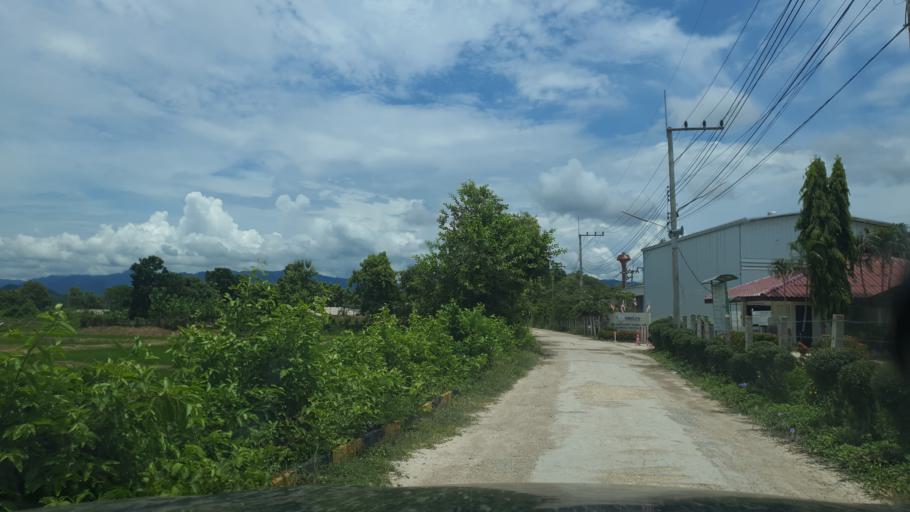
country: TH
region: Lampang
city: Sop Prap
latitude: 17.9415
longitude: 99.3524
